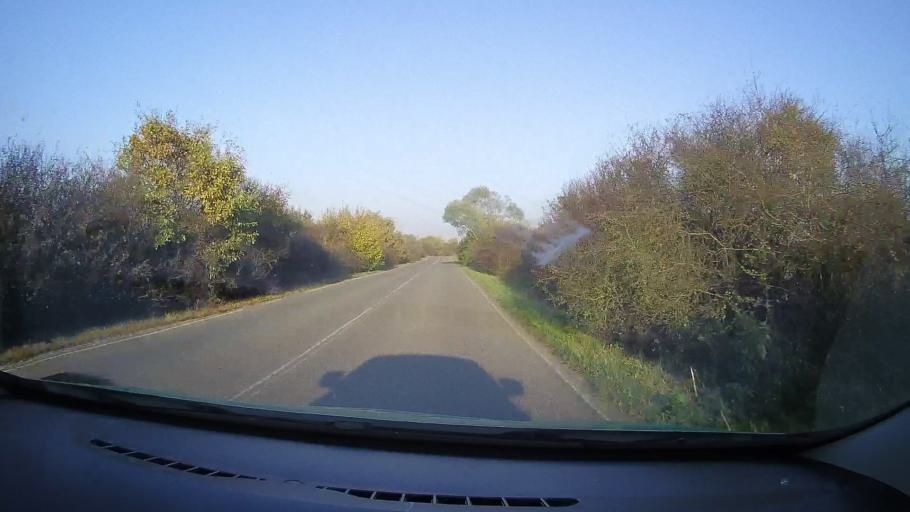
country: RO
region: Arad
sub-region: Comuna Silindia
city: Silindia
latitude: 46.3344
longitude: 21.8724
